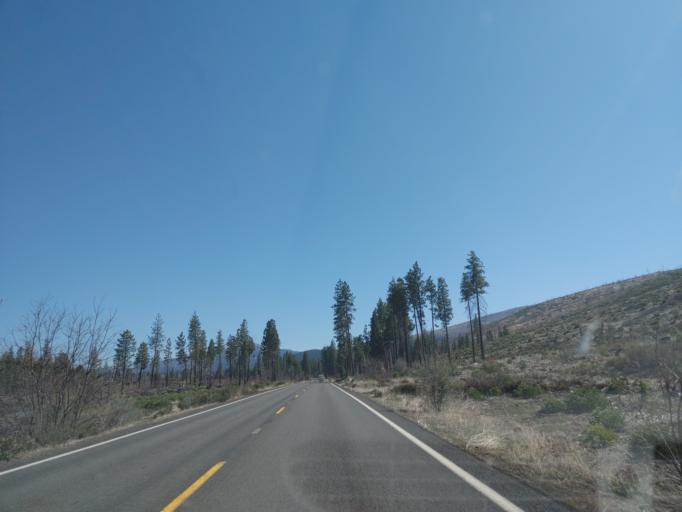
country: US
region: California
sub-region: Shasta County
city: Burney
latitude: 40.7868
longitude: -121.5056
